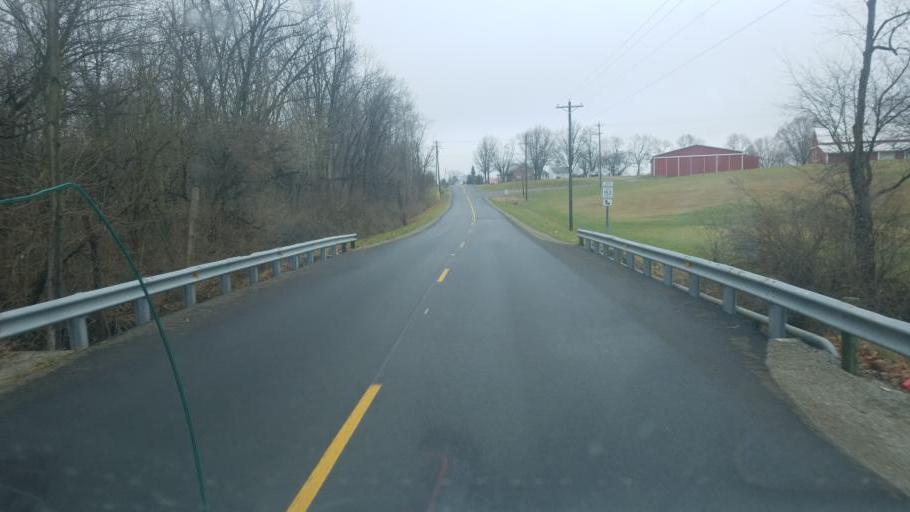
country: US
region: Ohio
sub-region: Champaign County
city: North Lewisburg
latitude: 40.2678
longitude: -83.5571
